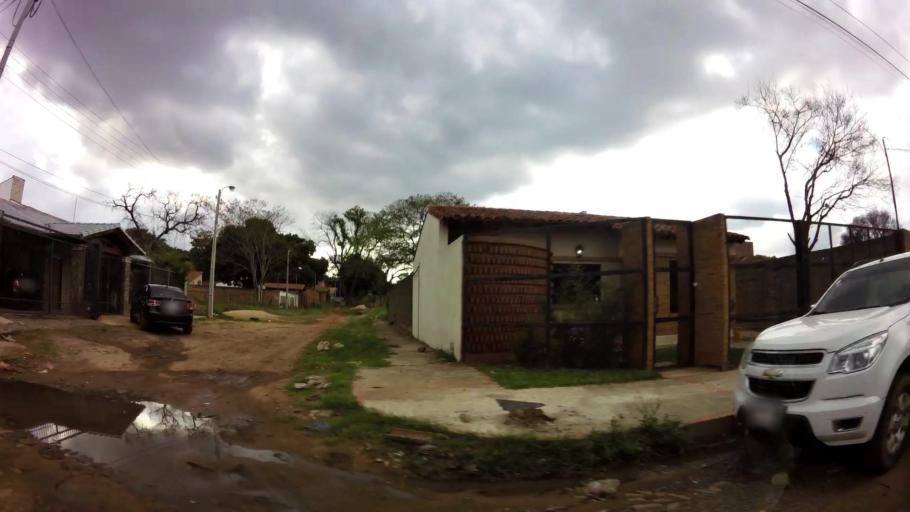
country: PY
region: Central
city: Fernando de la Mora
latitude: -25.3366
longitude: -57.5504
